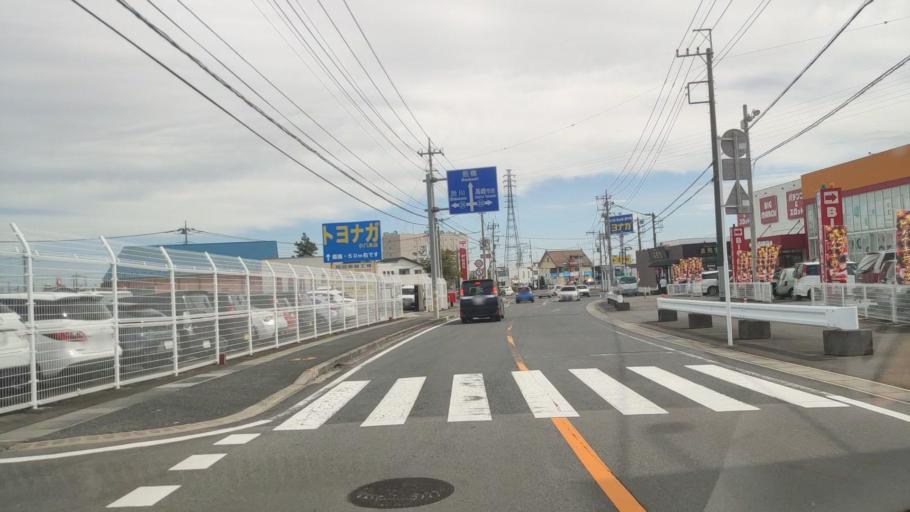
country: JP
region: Gunma
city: Takasaki
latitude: 36.3598
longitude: 139.0110
